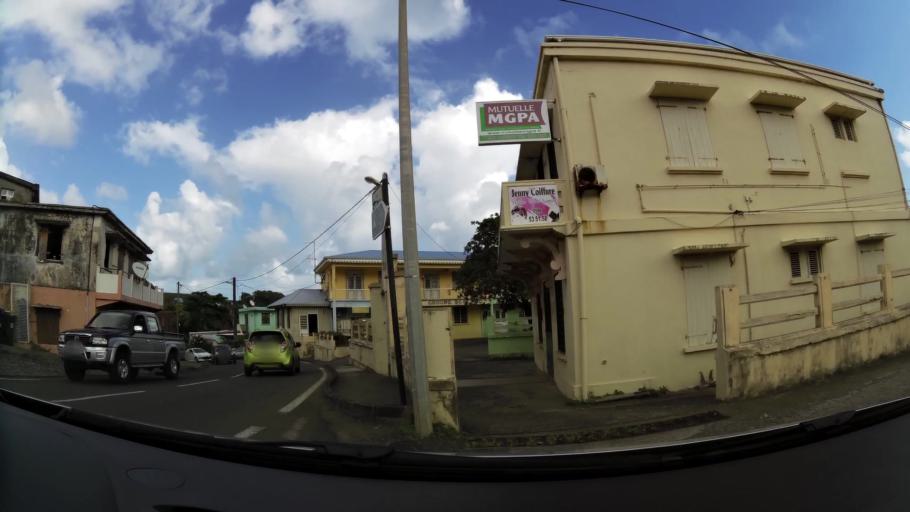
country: MQ
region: Martinique
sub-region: Martinique
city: Le Lorrain
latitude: 14.8221
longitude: -61.0305
